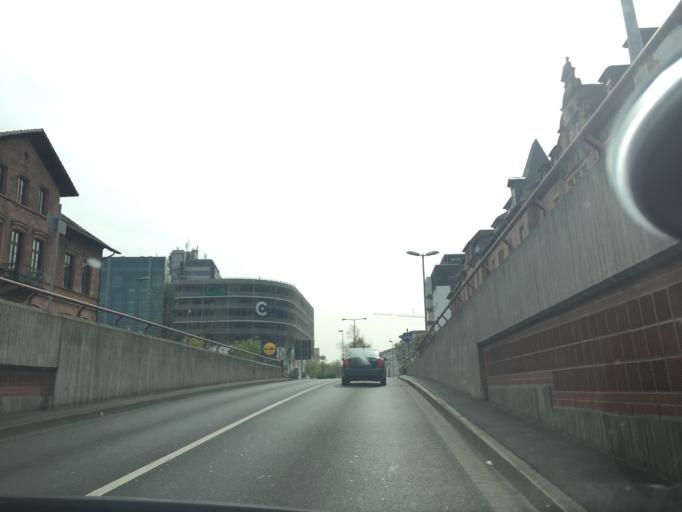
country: DE
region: Bavaria
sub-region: Regierungsbezirk Unterfranken
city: Aschaffenburg
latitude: 49.9803
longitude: 9.1533
